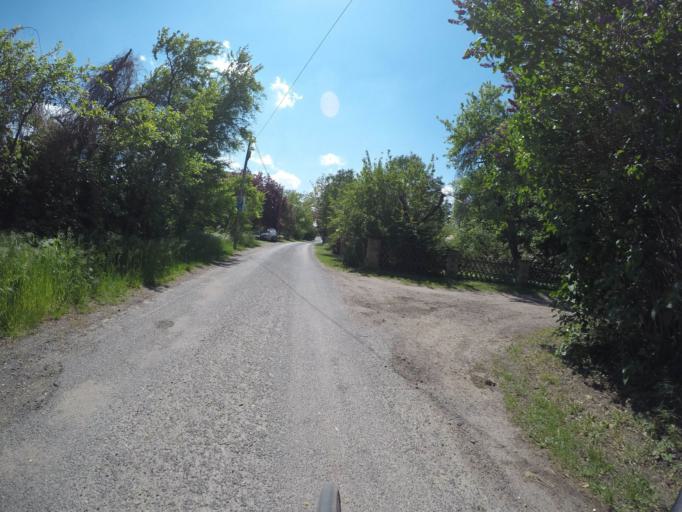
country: DE
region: Brandenburg
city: Werder
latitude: 52.4267
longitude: 12.9393
